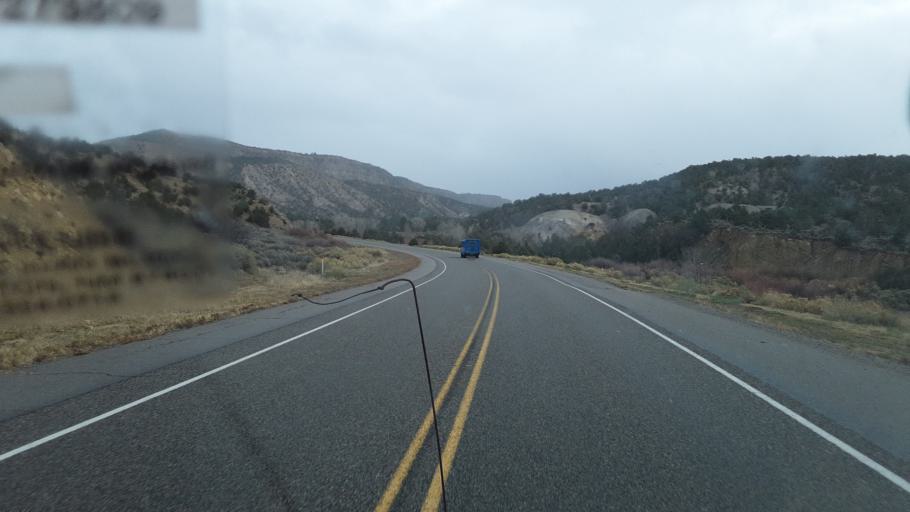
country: US
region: New Mexico
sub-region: Rio Arriba County
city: Santa Teresa
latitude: 36.3871
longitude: -106.4958
